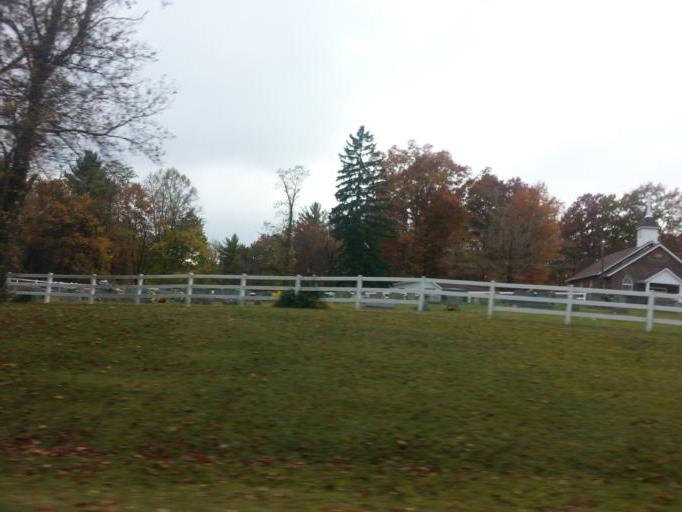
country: US
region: North Carolina
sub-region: Ashe County
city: West Jefferson
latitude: 36.2845
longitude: -81.4137
